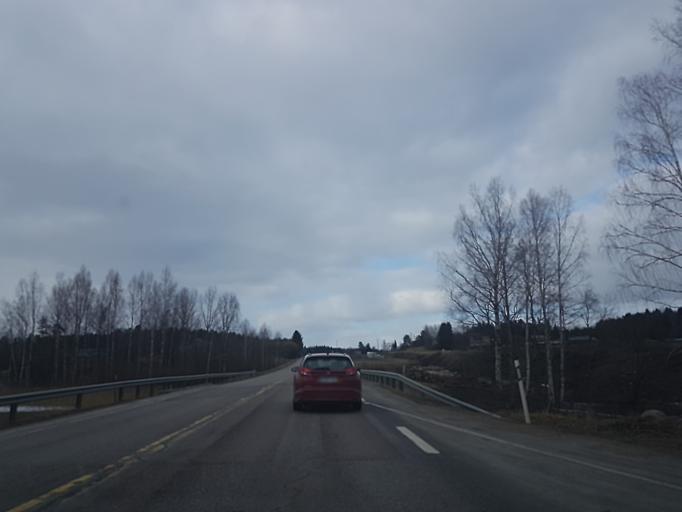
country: FI
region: South Karelia
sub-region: Imatra
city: Parikkala
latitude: 61.4946
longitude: 29.4851
